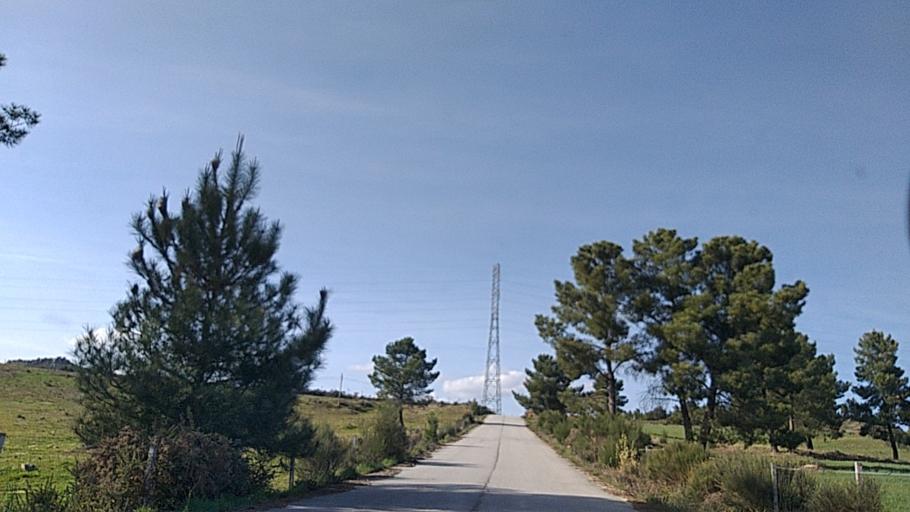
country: PT
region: Guarda
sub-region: Celorico da Beira
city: Celorico da Beira
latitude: 40.6493
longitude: -7.3951
